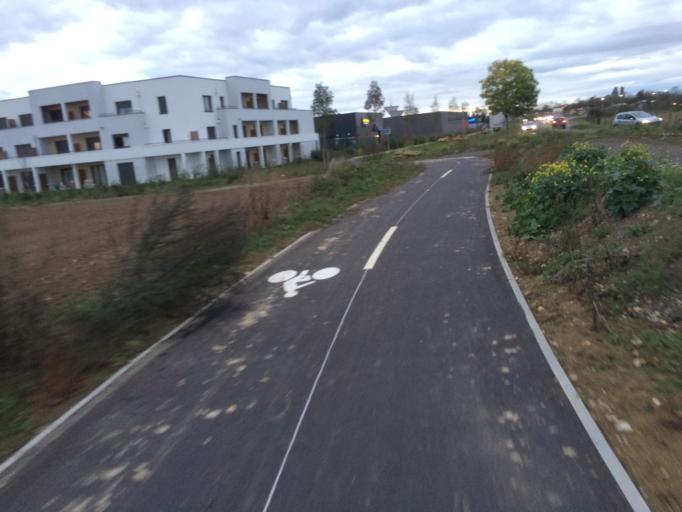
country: FR
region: Ile-de-France
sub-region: Departement de l'Essonne
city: Villejust
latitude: 48.6840
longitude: 2.2250
